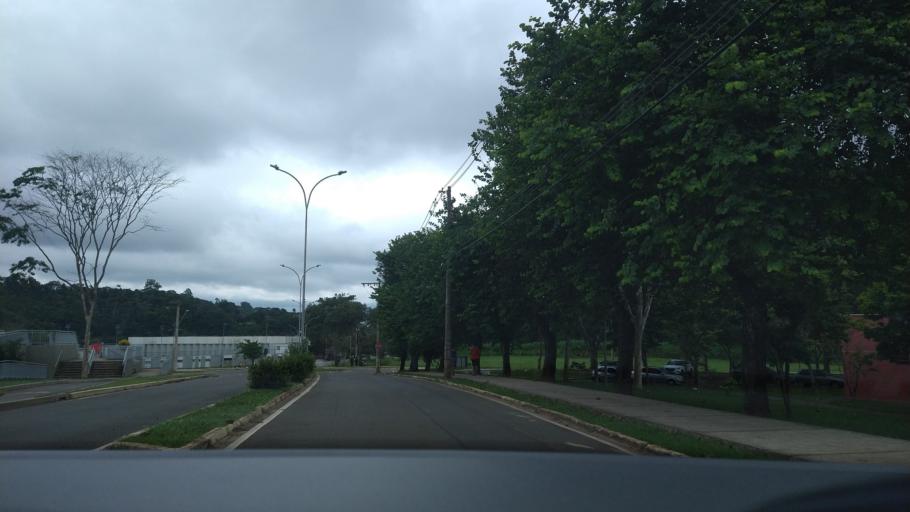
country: BR
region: Minas Gerais
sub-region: Vicosa
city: Vicosa
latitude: -20.7673
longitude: -42.8603
